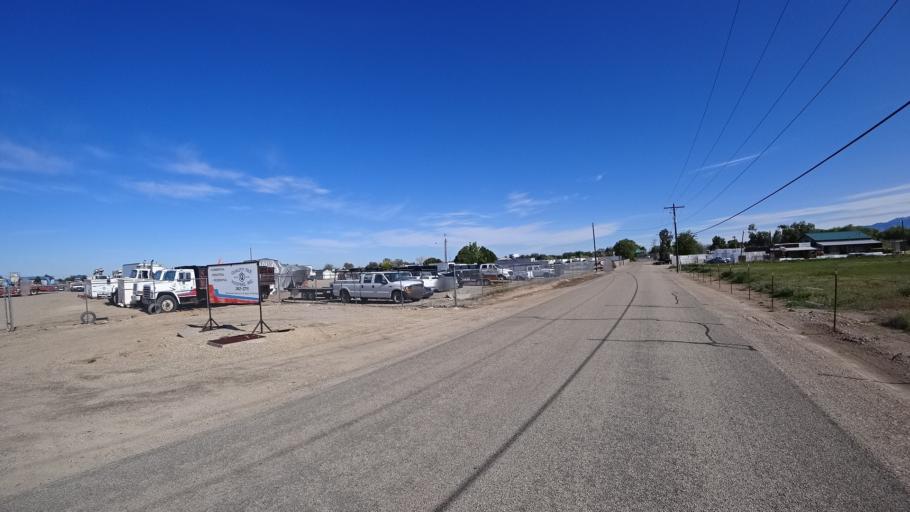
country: US
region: Idaho
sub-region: Ada County
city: Garden City
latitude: 43.5766
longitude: -116.2536
